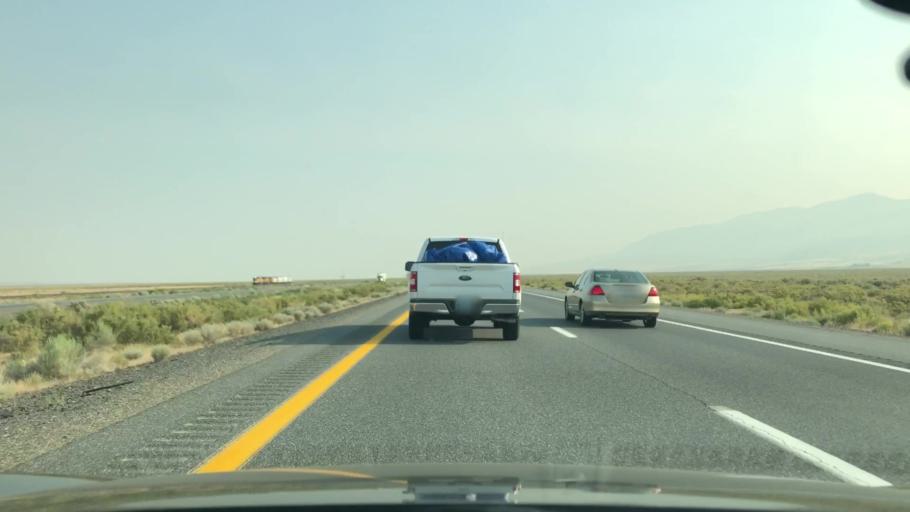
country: US
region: Nevada
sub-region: Pershing County
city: Lovelock
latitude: 40.3828
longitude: -118.3027
